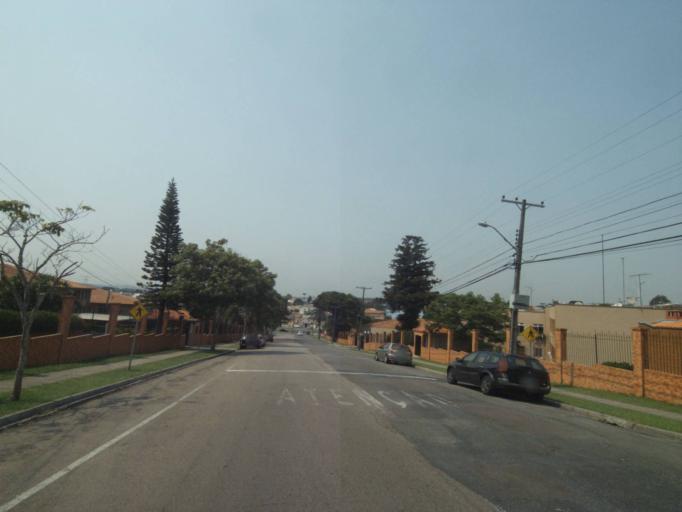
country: BR
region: Parana
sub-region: Sao Jose Dos Pinhais
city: Sao Jose dos Pinhais
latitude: -25.5259
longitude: -49.2405
